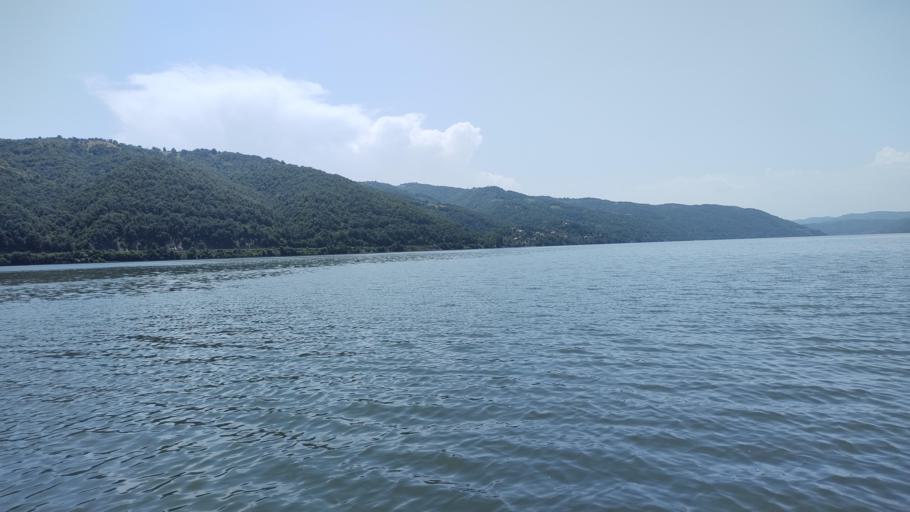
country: RO
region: Mehedinti
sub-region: Comuna Svinita
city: Svinita
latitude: 44.5185
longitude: 22.2006
